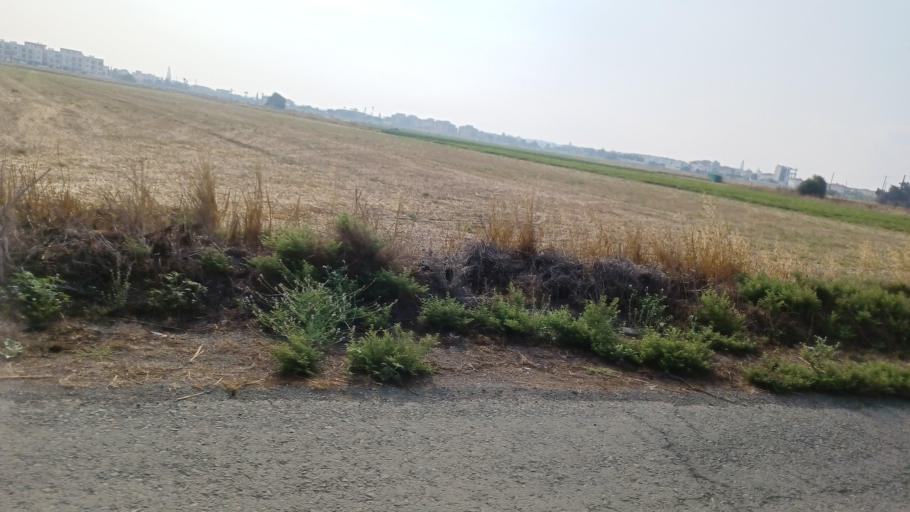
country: CY
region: Larnaka
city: Perivolia
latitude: 34.8240
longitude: 33.5784
